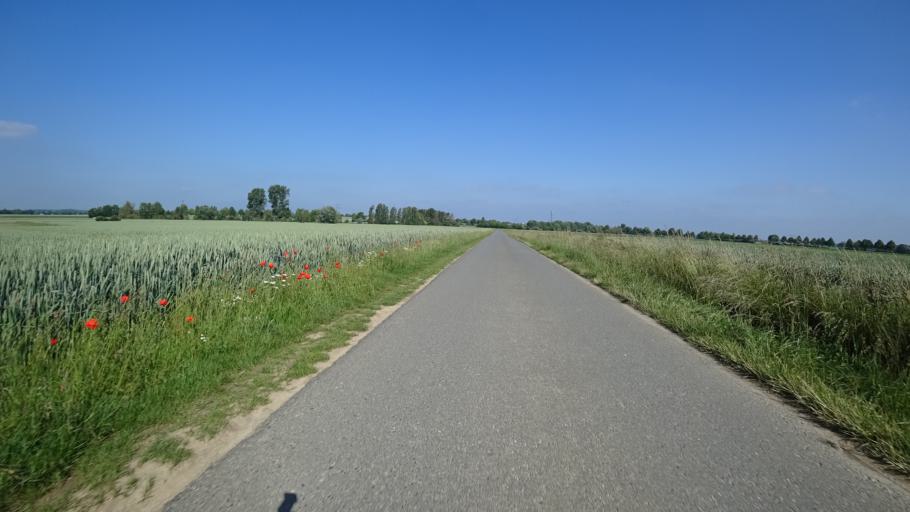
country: DE
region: North Rhine-Westphalia
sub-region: Regierungsbezirk Arnsberg
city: Lippstadt
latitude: 51.6426
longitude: 8.3787
